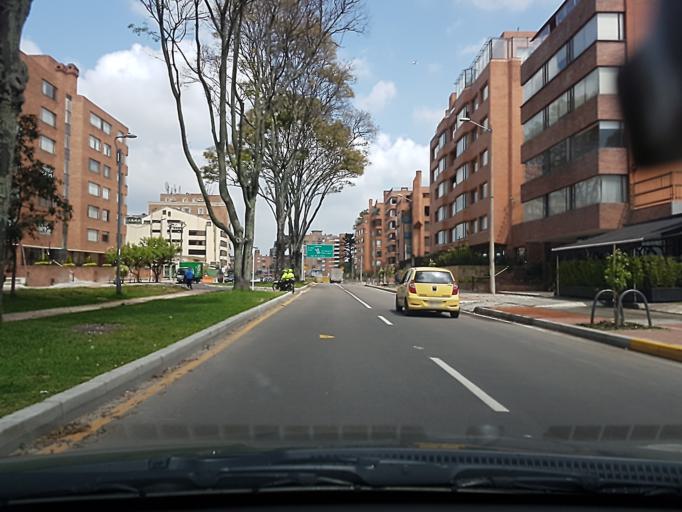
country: CO
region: Bogota D.C.
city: Barrio San Luis
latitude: 4.6803
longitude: -74.0519
